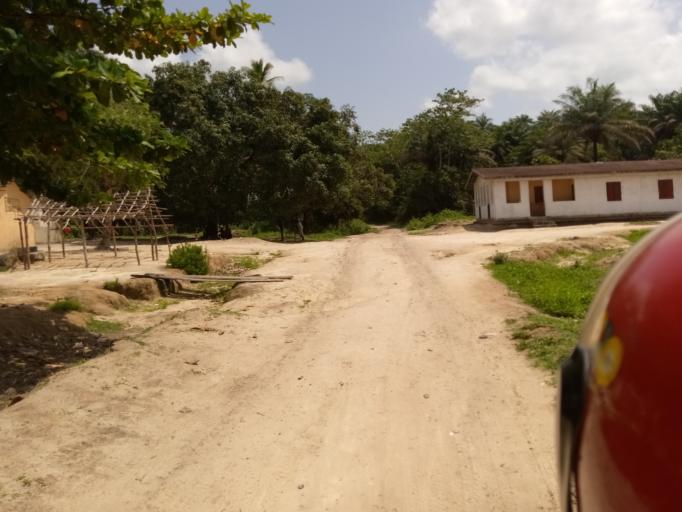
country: SL
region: Western Area
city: Waterloo
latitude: 8.3641
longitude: -13.0013
